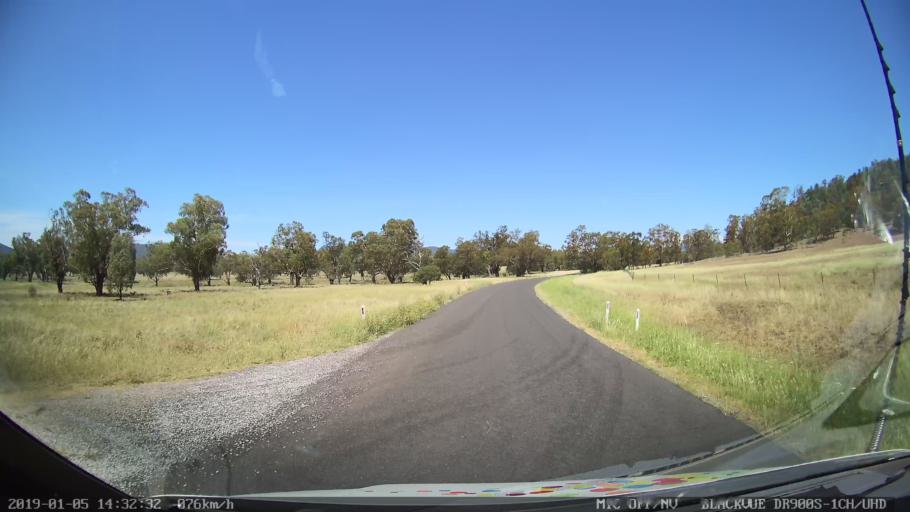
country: AU
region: New South Wales
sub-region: Tamworth Municipality
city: Phillip
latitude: -31.2209
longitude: 150.6195
